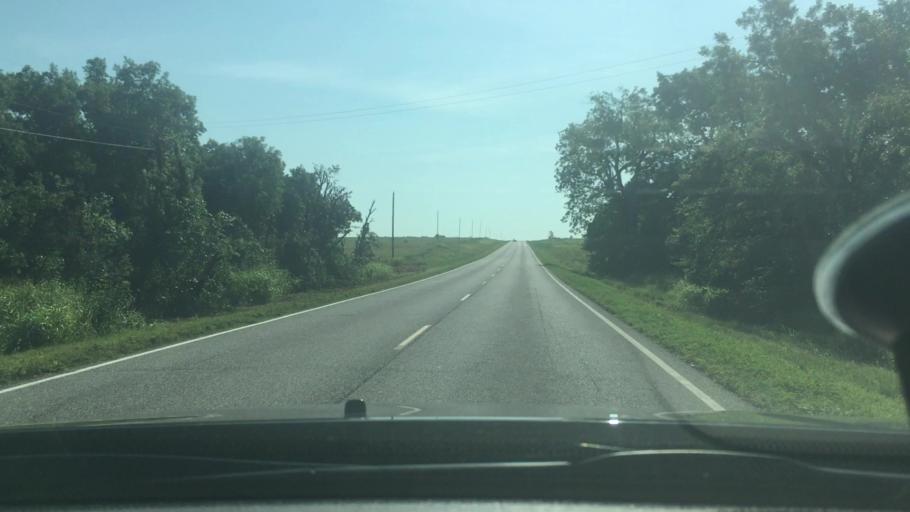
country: US
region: Oklahoma
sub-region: Garvin County
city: Pauls Valley
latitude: 34.6520
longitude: -97.3250
